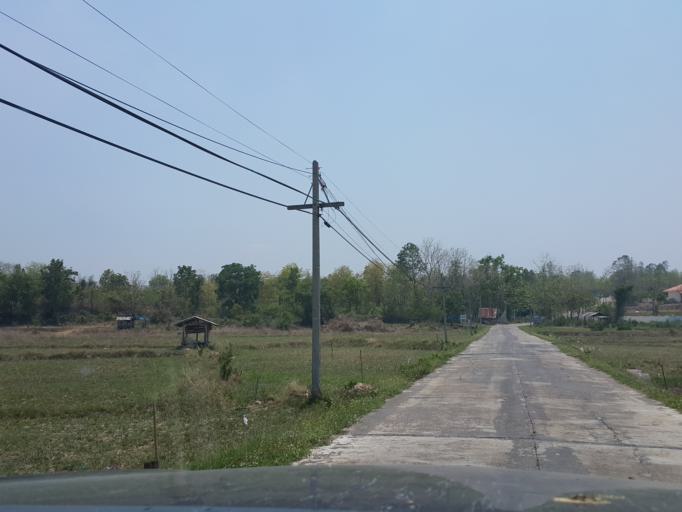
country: TH
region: Lampang
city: Thoen
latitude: 17.6380
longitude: 99.2535
